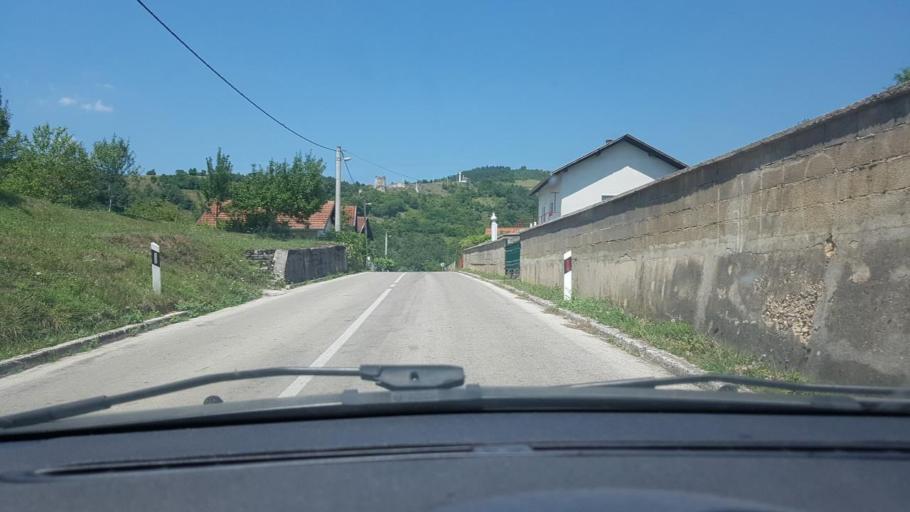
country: BA
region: Federation of Bosnia and Herzegovina
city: Orasac
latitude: 44.6205
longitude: 16.0692
